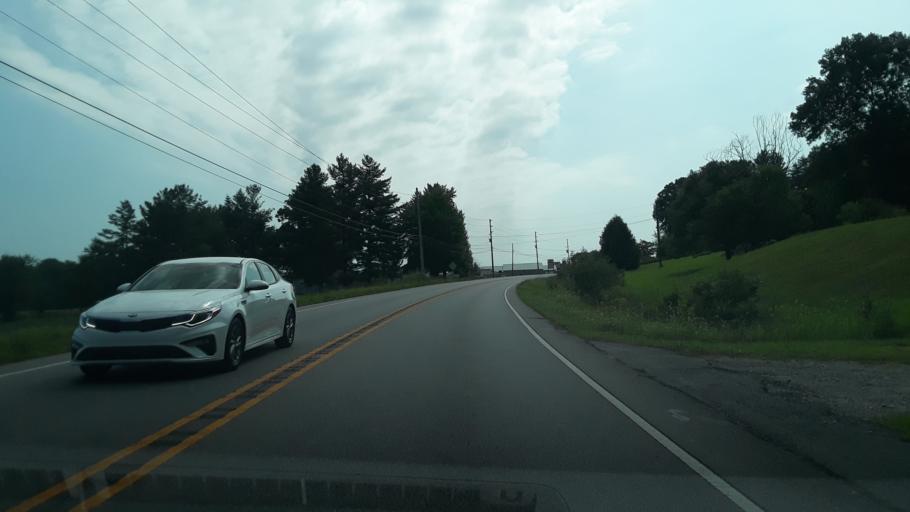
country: US
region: Indiana
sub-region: Clark County
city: Sellersburg
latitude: 38.4453
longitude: -85.8620
